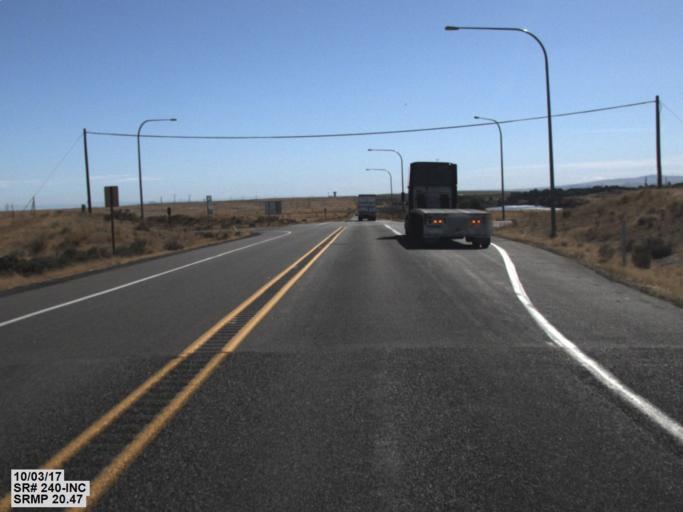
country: US
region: Washington
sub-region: Benton County
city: West Richland
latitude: 46.3834
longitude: -119.4230
